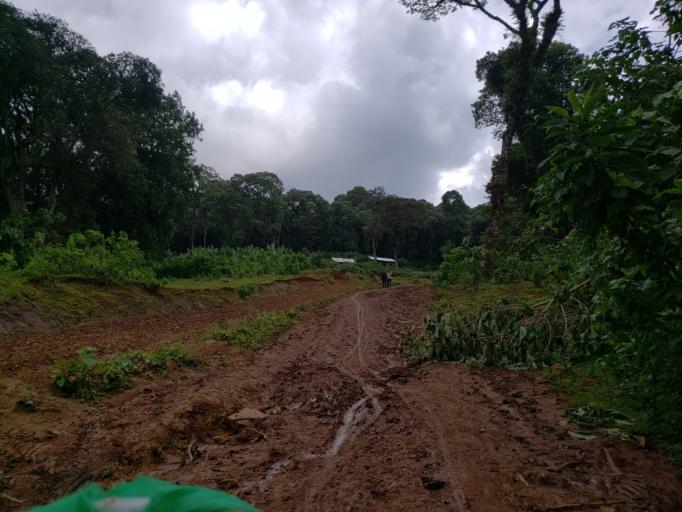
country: ET
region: Oromiya
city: Dodola
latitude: 6.4892
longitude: 39.4966
